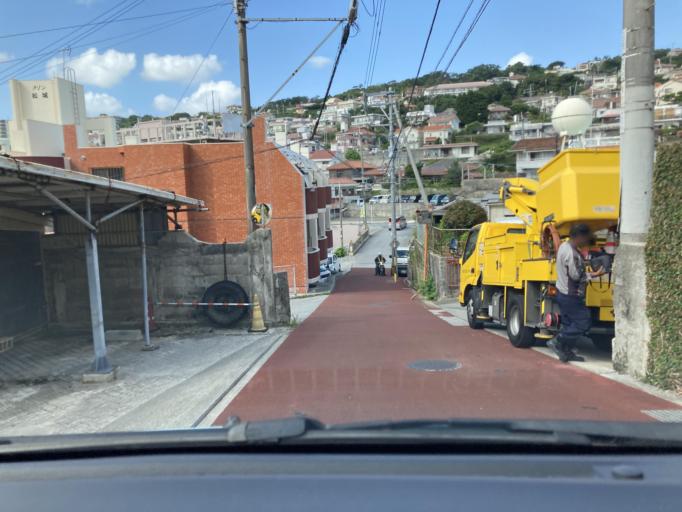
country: JP
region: Okinawa
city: Naha-shi
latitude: 26.2136
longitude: 127.7139
